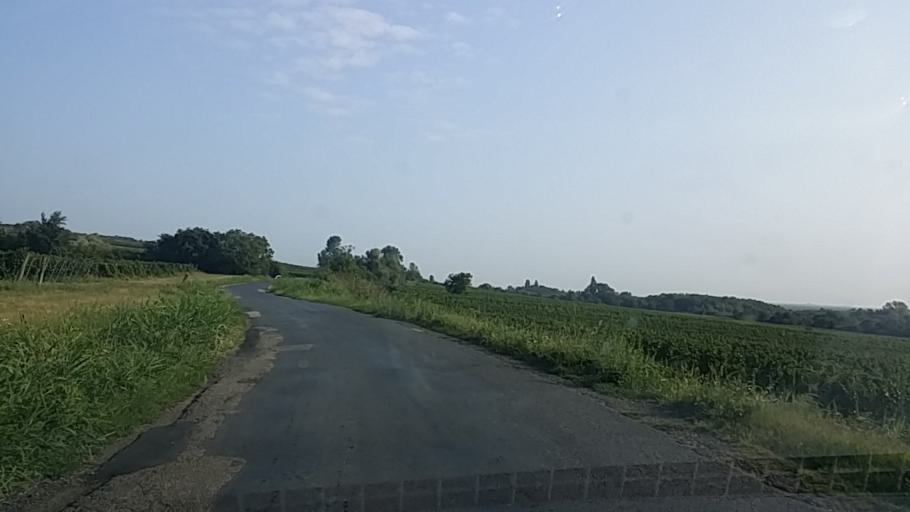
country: HU
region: Gyor-Moson-Sopron
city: Fertorakos
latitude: 47.6636
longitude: 16.6687
